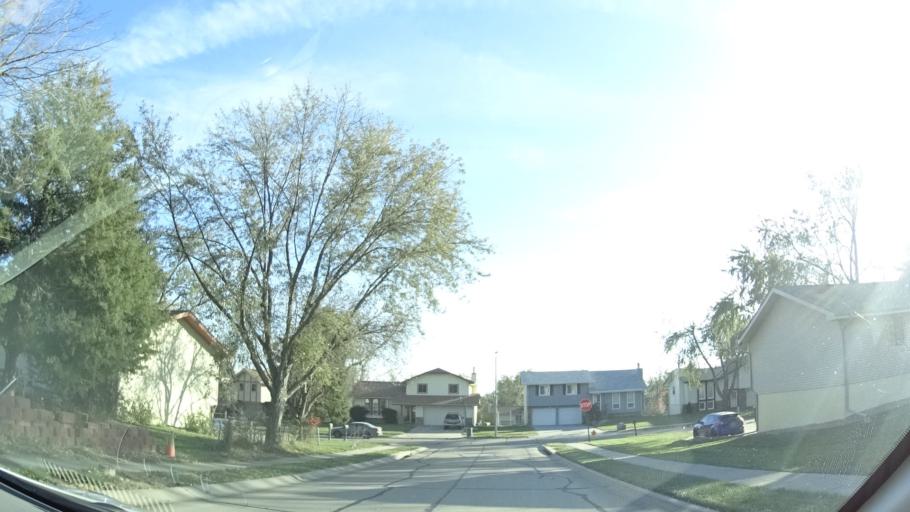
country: US
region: Nebraska
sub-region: Sarpy County
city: Offutt Air Force Base
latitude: 41.1328
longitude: -95.9498
